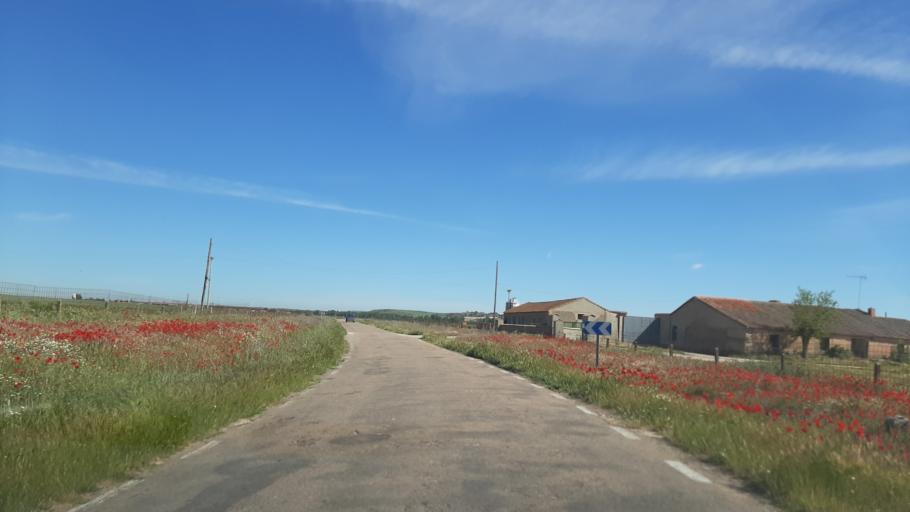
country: ES
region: Castille and Leon
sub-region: Provincia de Salamanca
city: Gajates
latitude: 40.7963
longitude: -5.3729
